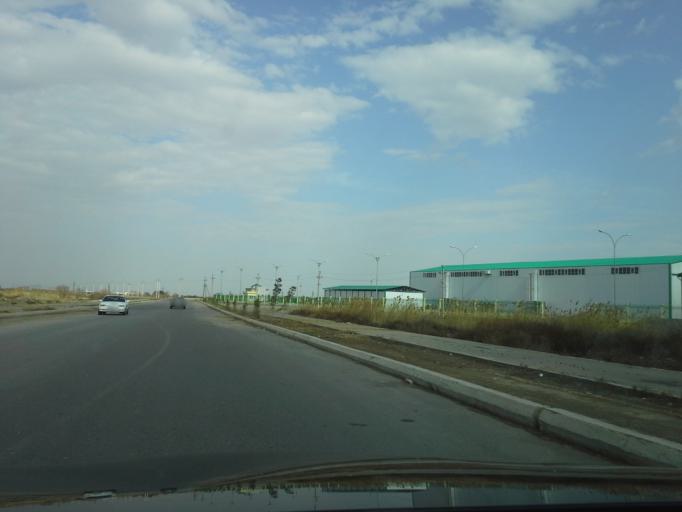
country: TM
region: Ahal
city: Abadan
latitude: 37.9902
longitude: 58.2773
